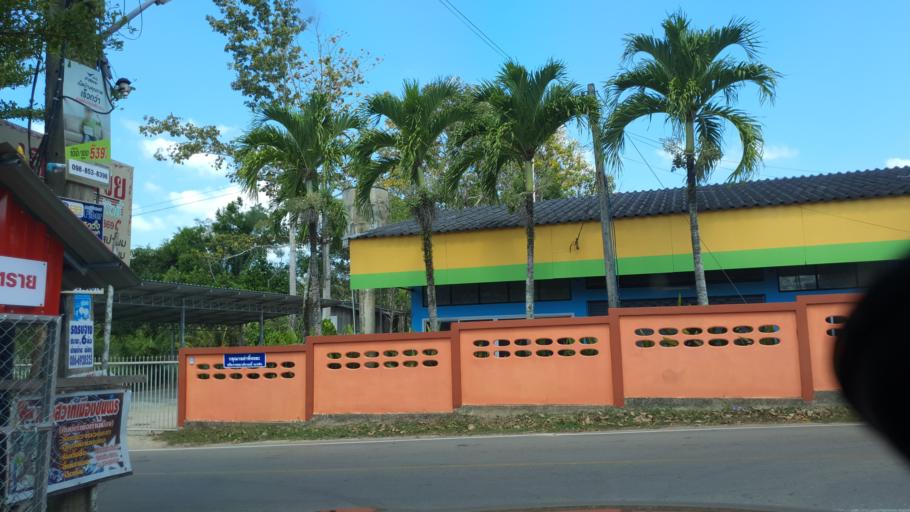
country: TH
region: Krabi
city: Nuea Khlong
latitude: 8.0838
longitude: 98.9888
